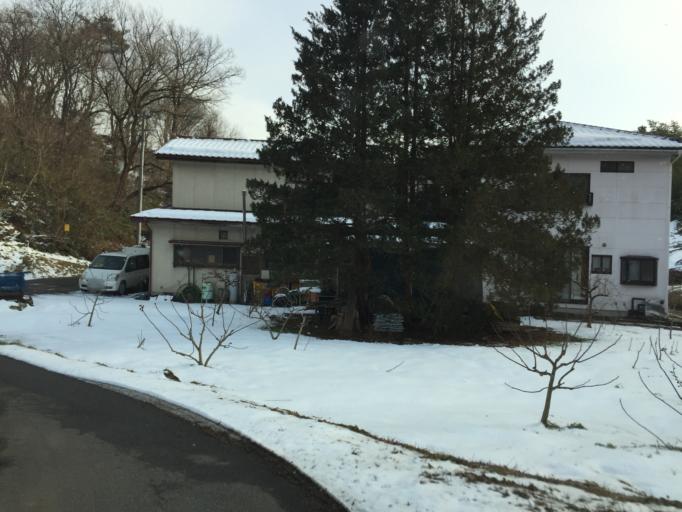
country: JP
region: Fukushima
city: Fukushima-shi
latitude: 37.8367
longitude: 140.4580
